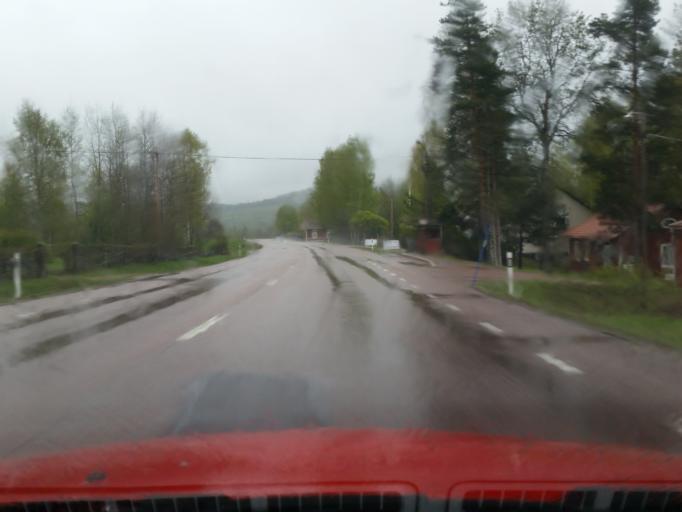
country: SE
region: Dalarna
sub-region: Gagnefs Kommun
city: Djuras
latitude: 60.5518
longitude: 15.2557
